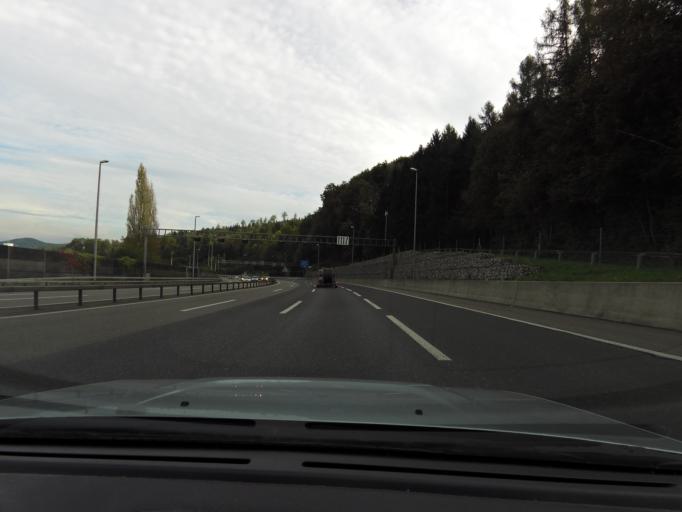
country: CH
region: Aargau
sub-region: Bezirk Baden
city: Wettingen
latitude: 47.4550
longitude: 8.3084
